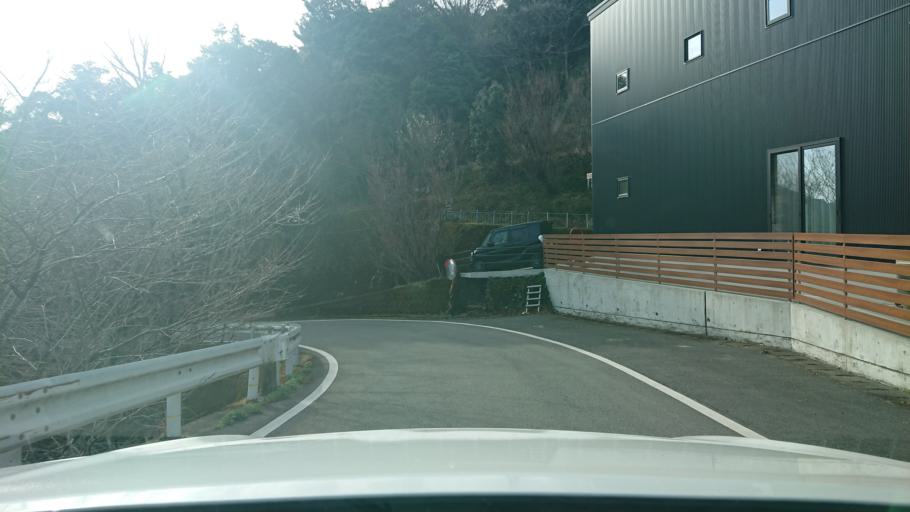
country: JP
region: Tokushima
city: Ishii
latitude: 33.9147
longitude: 134.4118
